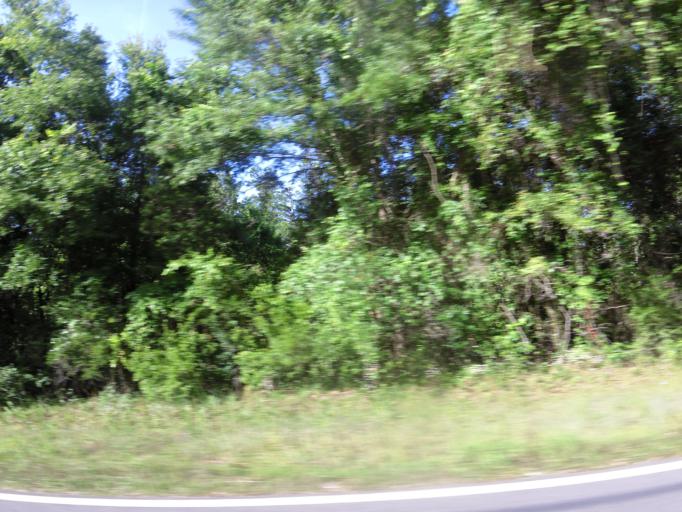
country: US
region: Florida
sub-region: Nassau County
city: Nassau Village-Ratliff
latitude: 30.4806
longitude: -81.8449
